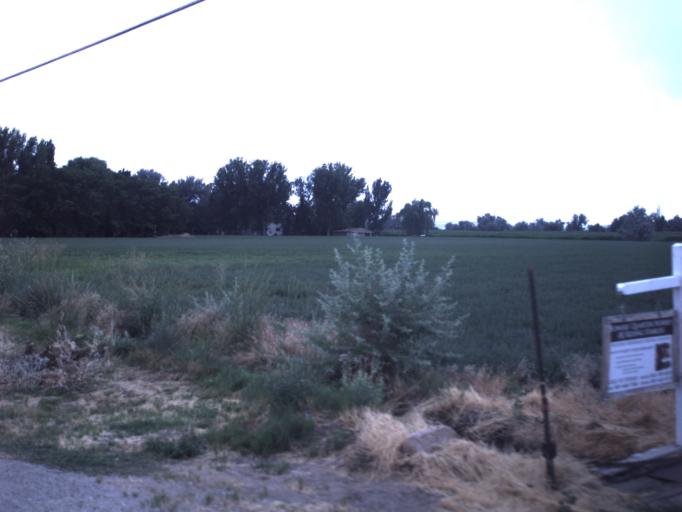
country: US
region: Utah
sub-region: Davis County
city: West Point
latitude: 41.1134
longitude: -112.1125
